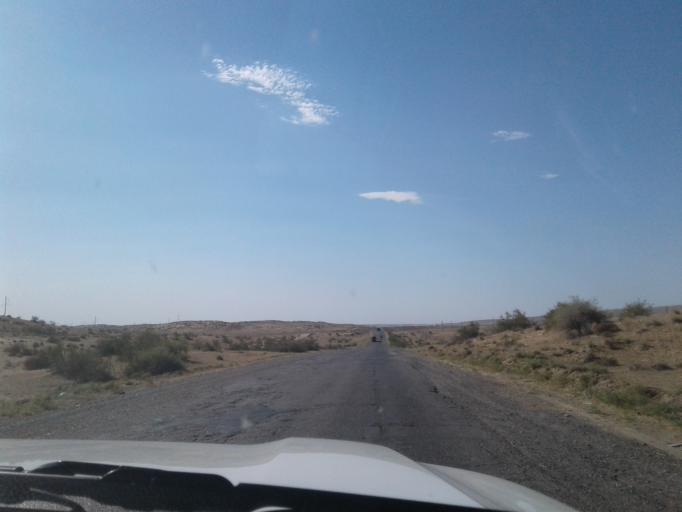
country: TM
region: Mary
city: Yoloeten
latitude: 36.5580
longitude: 62.5459
